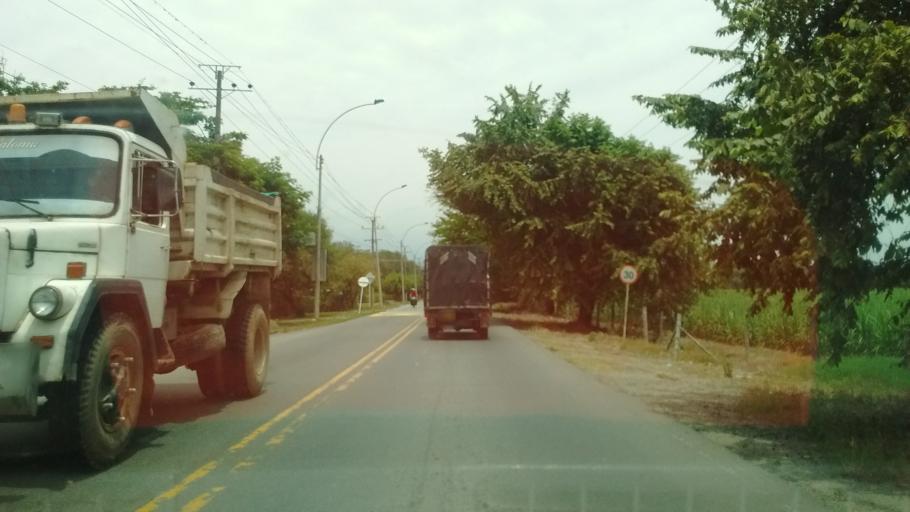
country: CO
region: Valle del Cauca
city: Jamundi
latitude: 3.3200
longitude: -76.4954
